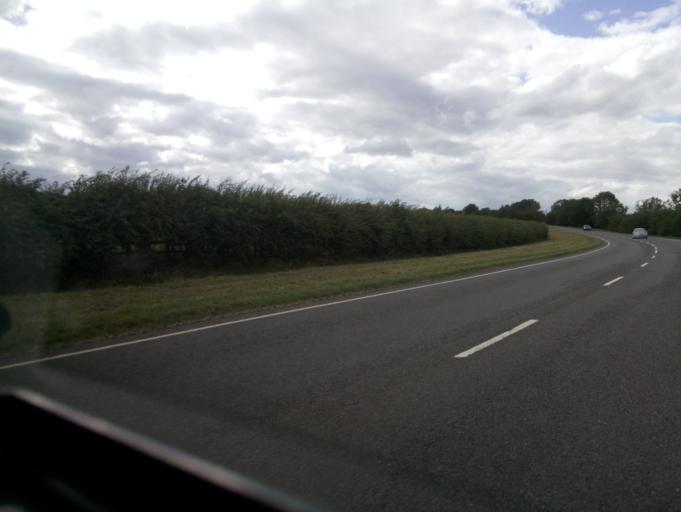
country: GB
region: England
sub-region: Leicestershire
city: Measham
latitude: 52.6368
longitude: -1.4946
